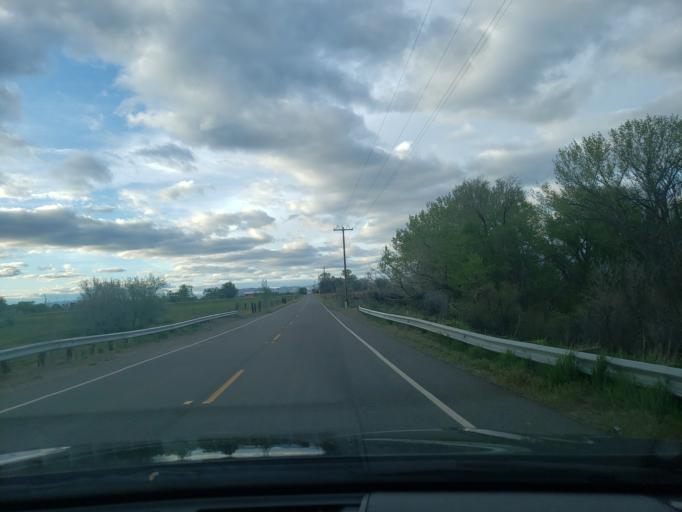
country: US
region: Colorado
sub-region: Mesa County
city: Fruita
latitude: 39.1969
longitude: -108.7293
